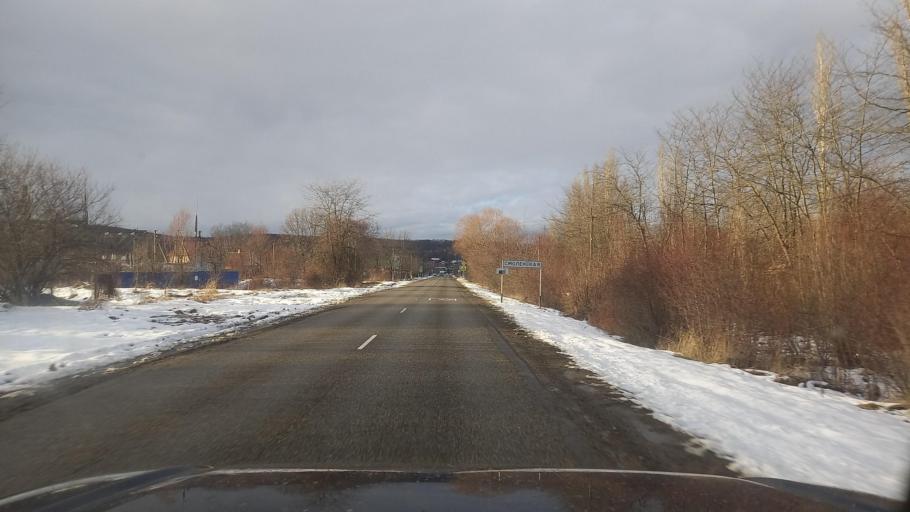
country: RU
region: Krasnodarskiy
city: Smolenskaya
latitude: 44.7810
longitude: 38.8087
